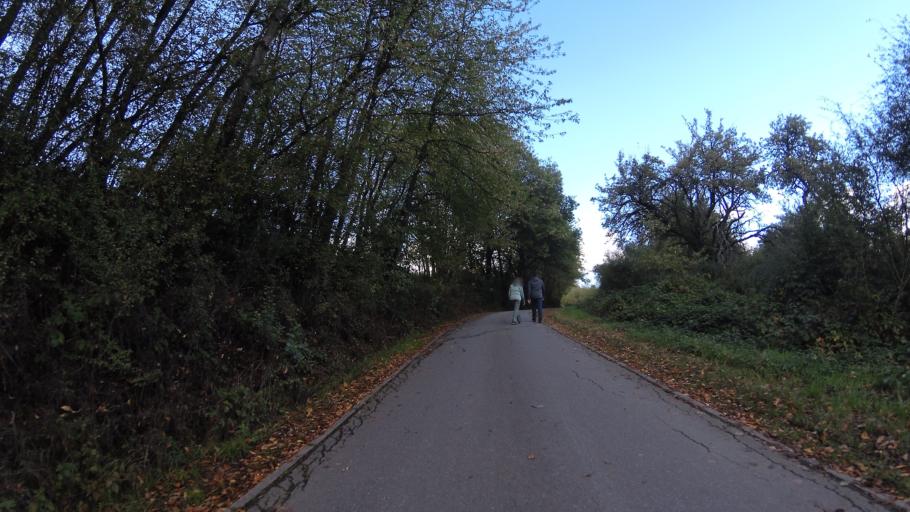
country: DE
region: Saarland
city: Tholey
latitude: 49.4743
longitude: 7.0405
